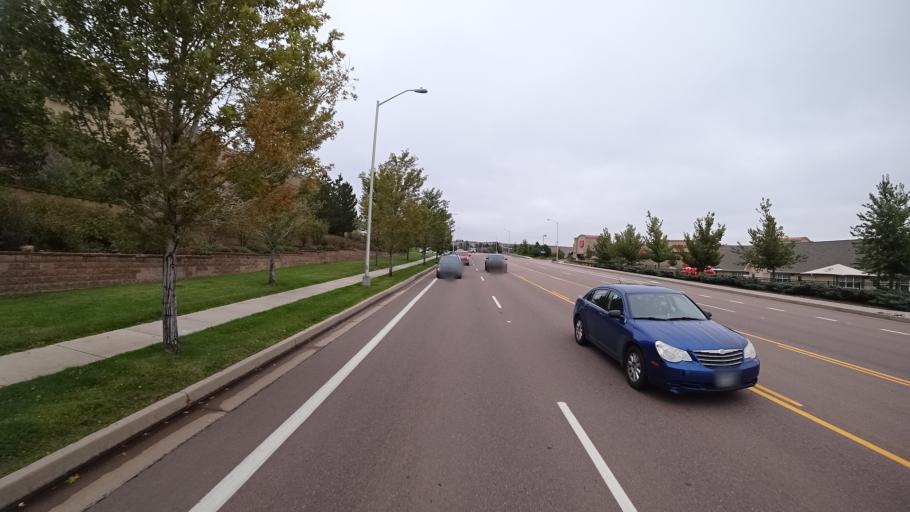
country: US
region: Colorado
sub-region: El Paso County
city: Cimarron Hills
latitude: 38.8879
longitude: -104.7141
